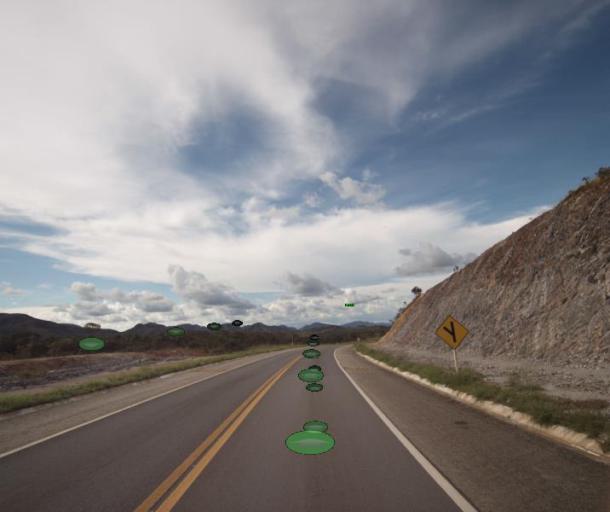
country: BR
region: Goias
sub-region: Barro Alto
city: Barro Alto
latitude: -15.1038
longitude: -48.7499
